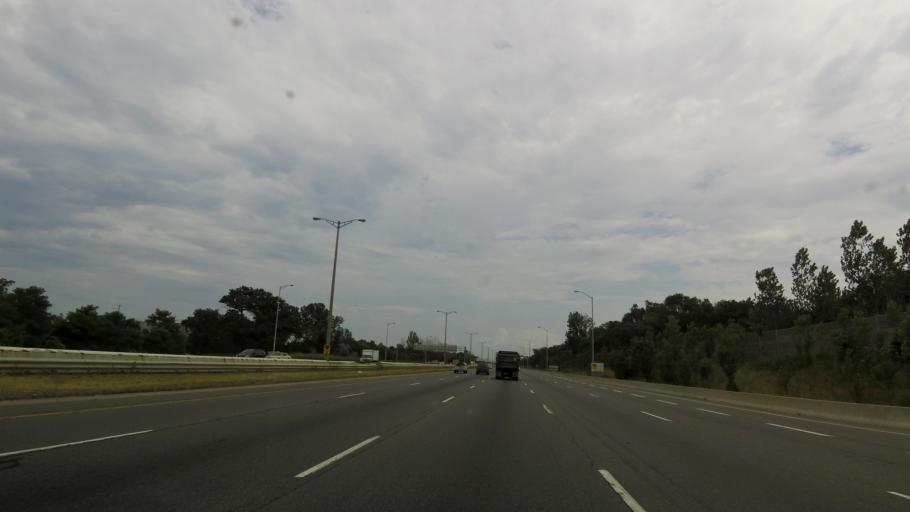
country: CA
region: Ontario
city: Burlington
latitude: 43.3230
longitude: -79.8208
